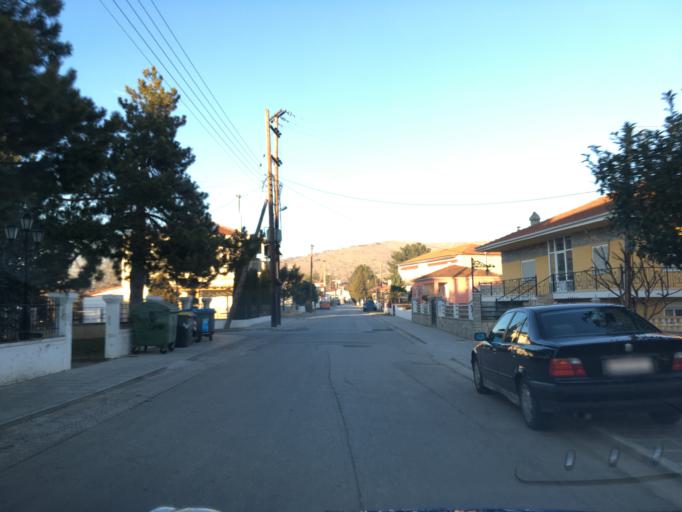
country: GR
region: West Macedonia
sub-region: Nomos Kozanis
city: Kozani
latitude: 40.2895
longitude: 21.7345
